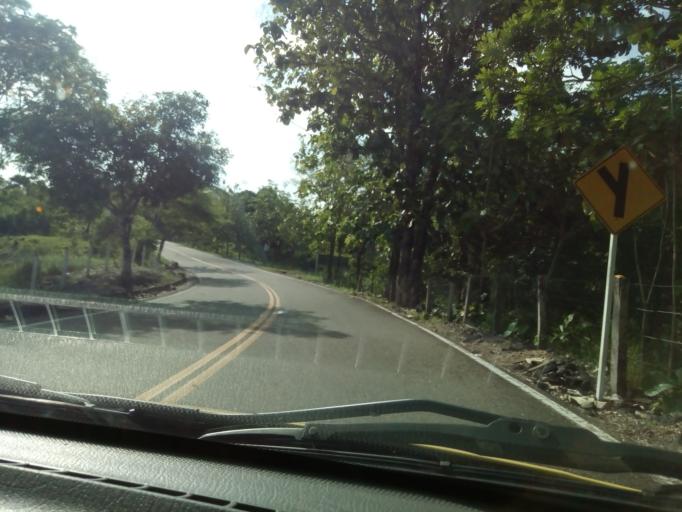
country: CO
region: Boyaca
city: Puerto Boyaca
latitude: 5.9551
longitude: -74.4846
